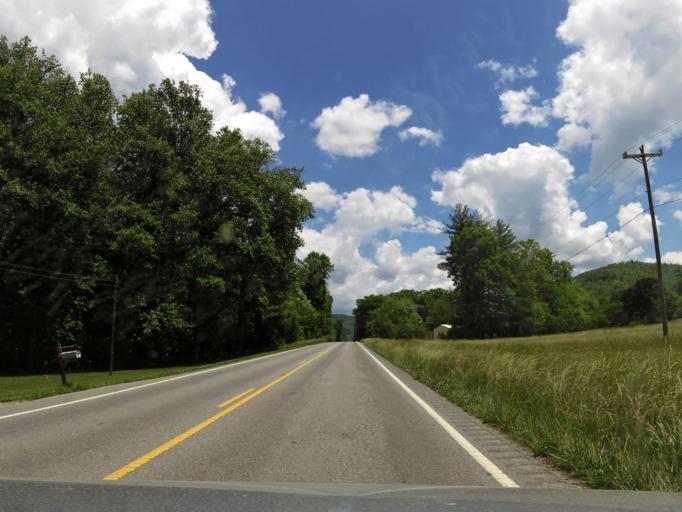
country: US
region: North Carolina
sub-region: Graham County
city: Robbinsville
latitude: 35.2950
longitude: -83.7891
